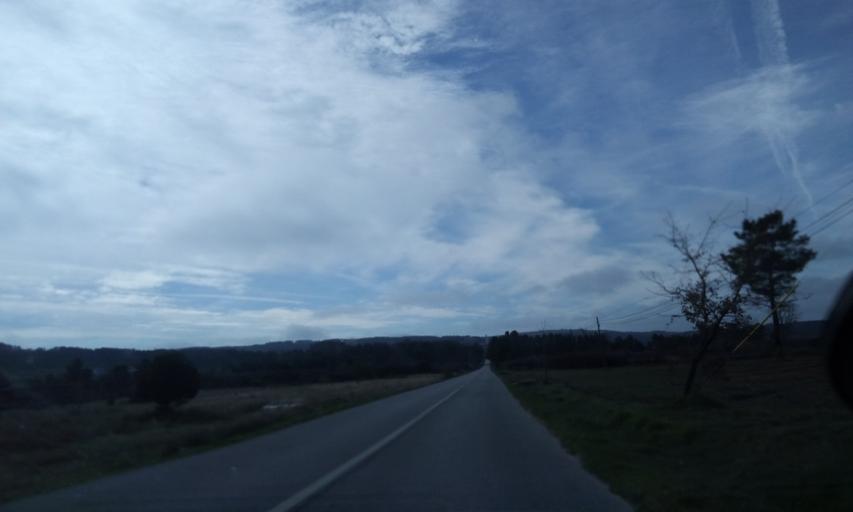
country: PT
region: Guarda
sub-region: Fornos de Algodres
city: Fornos de Algodres
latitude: 40.6716
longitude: -7.5288
